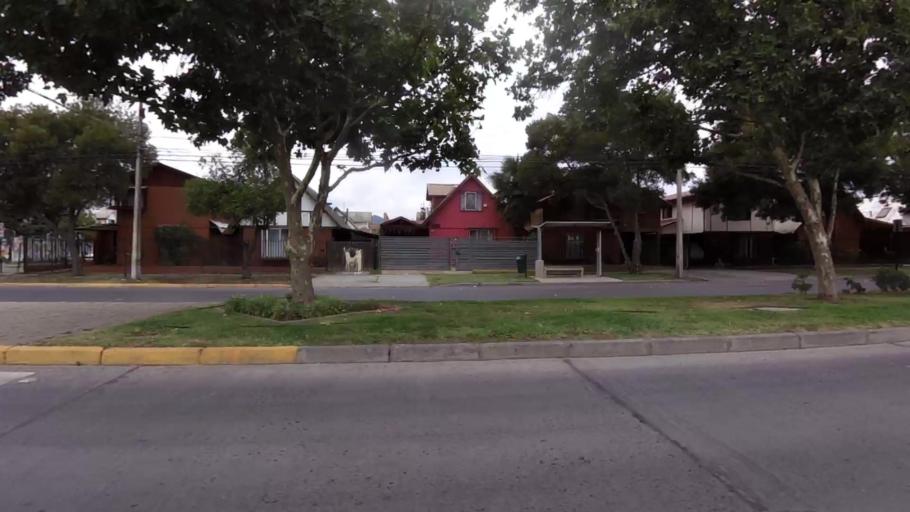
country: CL
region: O'Higgins
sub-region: Provincia de Cachapoal
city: Rancagua
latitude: -34.1499
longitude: -70.7309
